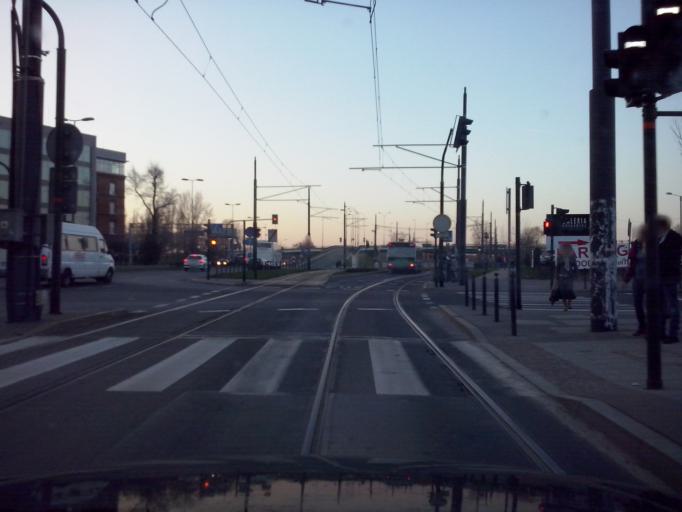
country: PL
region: Lesser Poland Voivodeship
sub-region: Krakow
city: Krakow
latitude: 50.0712
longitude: 19.9451
